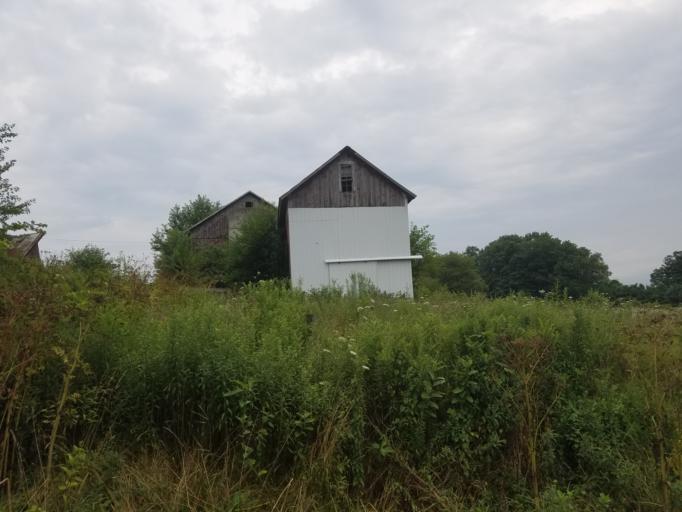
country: US
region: Ohio
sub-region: Knox County
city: Fredericktown
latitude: 40.5518
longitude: -82.6261
